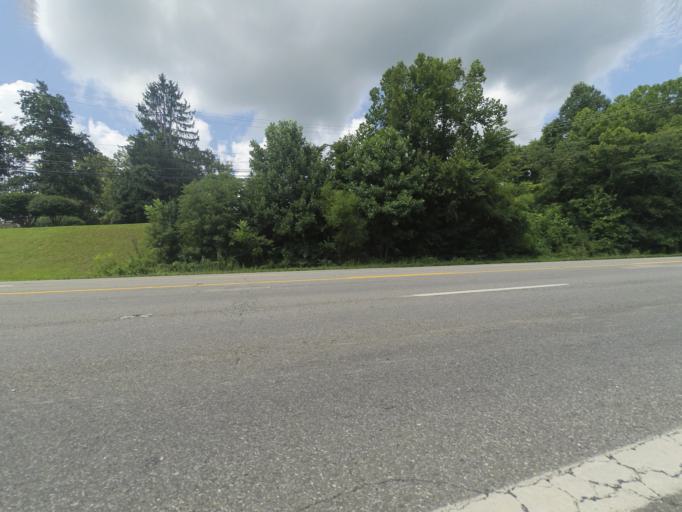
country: US
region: West Virginia
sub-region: Cabell County
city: Pea Ridge
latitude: 38.4102
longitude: -82.3302
